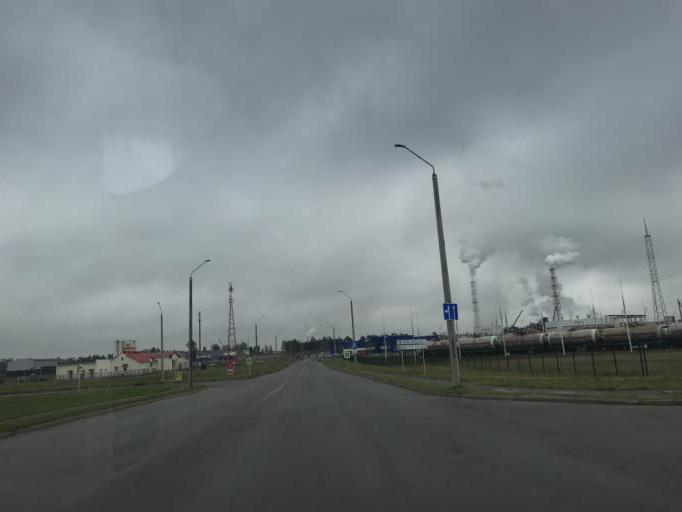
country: BY
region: Mogilev
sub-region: Mahilyowski Rayon
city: Veyno
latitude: 53.8288
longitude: 30.3475
